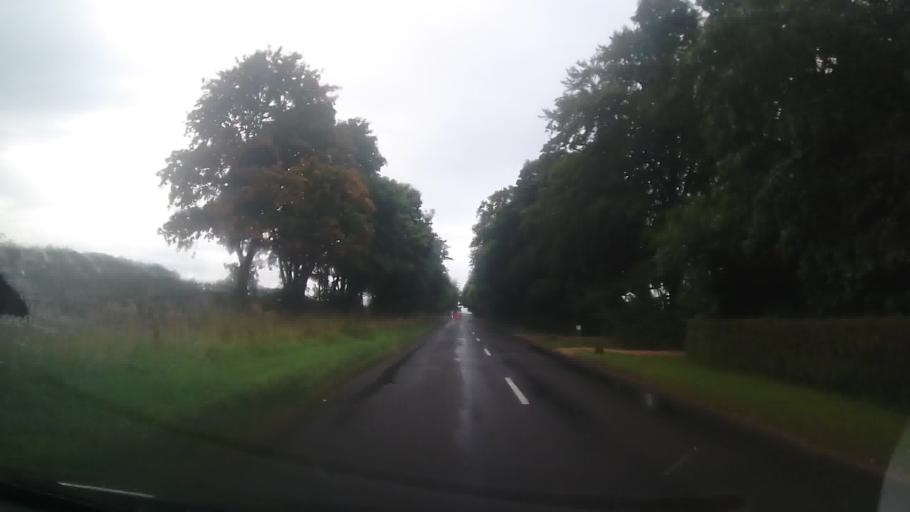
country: GB
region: England
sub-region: Oxfordshire
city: Stonesfield
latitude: 51.8684
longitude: -1.3913
